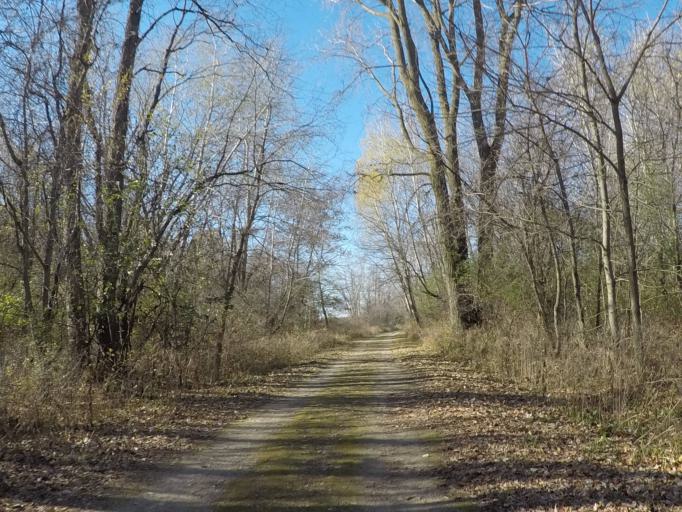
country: US
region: Wisconsin
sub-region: Jefferson County
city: Cambridge
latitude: 43.0450
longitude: -89.0194
